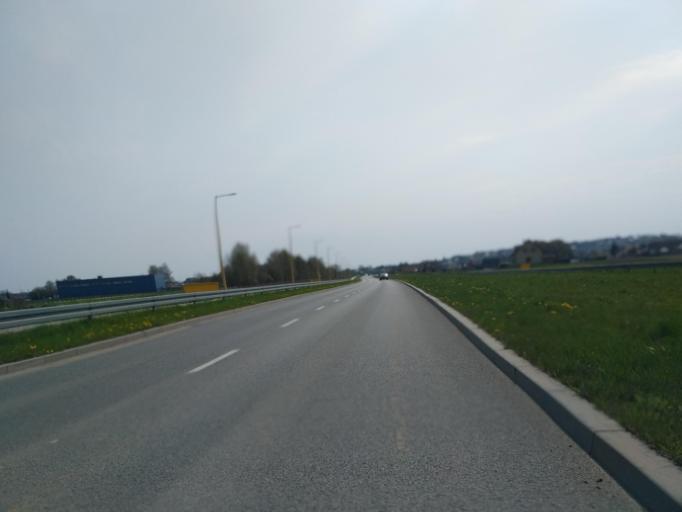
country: PL
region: Subcarpathian Voivodeship
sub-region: Krosno
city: Krosno
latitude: 49.6741
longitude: 21.7408
